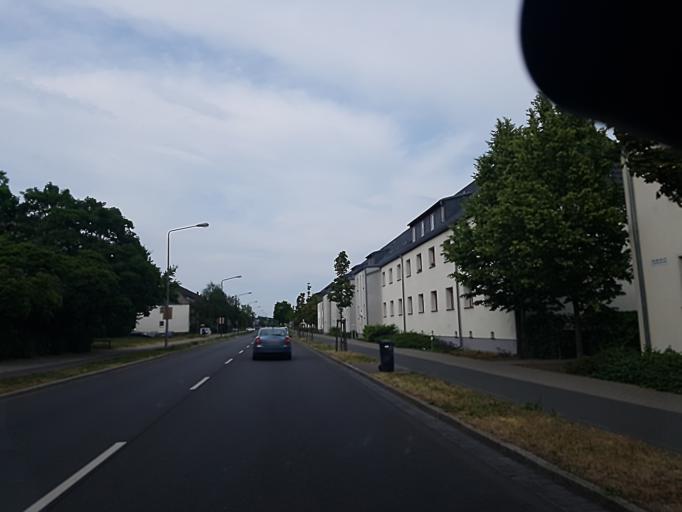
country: DE
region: Saxony-Anhalt
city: Wittenburg
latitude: 51.8766
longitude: 12.6500
